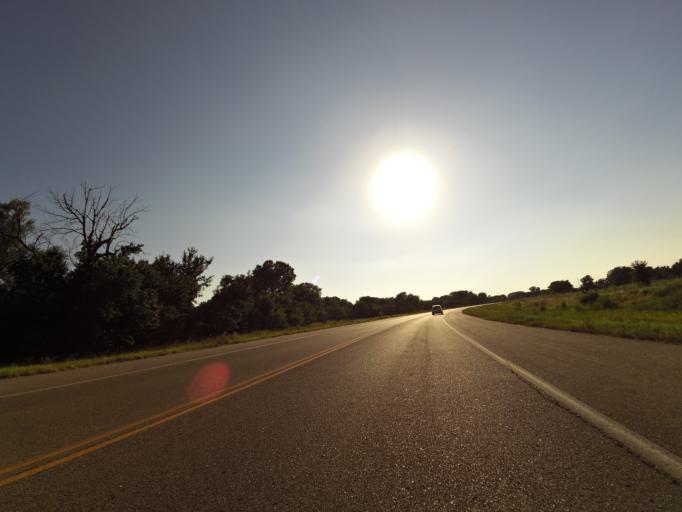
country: US
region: Kansas
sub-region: Reno County
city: Buhler
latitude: 38.1486
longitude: -97.8407
